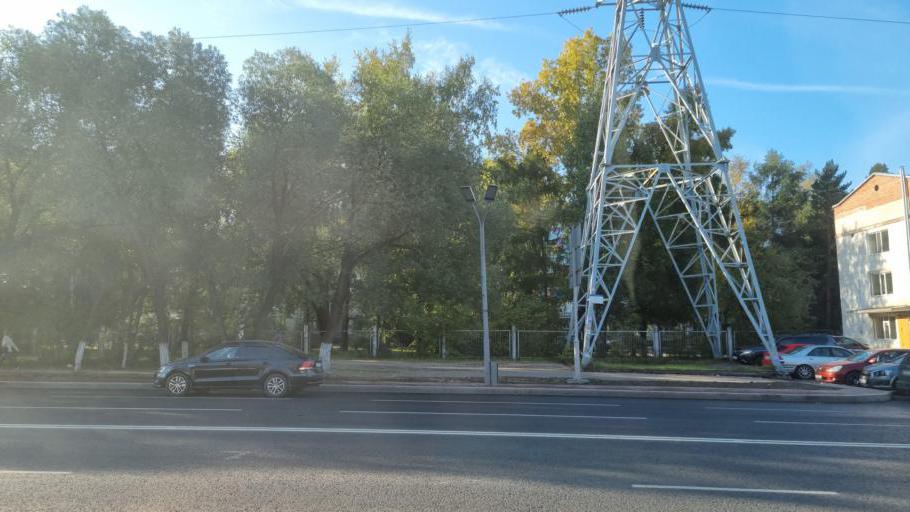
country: RU
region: Tomsk
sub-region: Tomskiy Rayon
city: Tomsk
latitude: 56.4553
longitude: 84.9616
